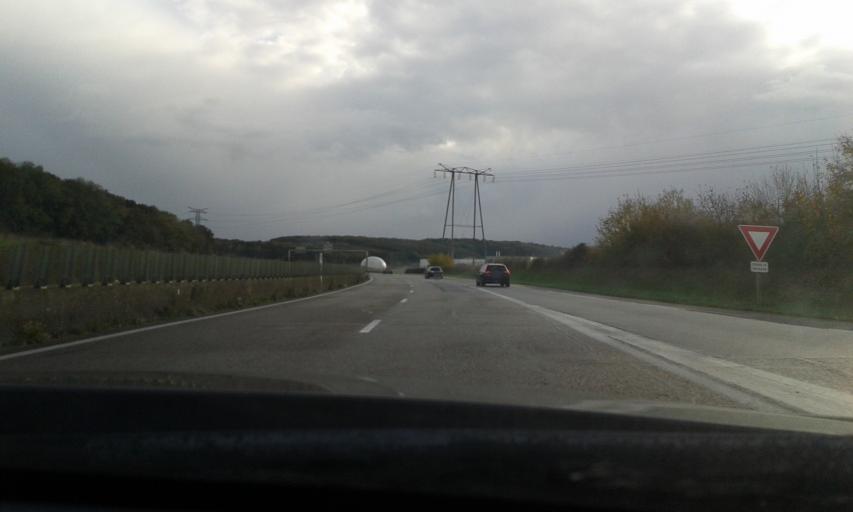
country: FR
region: Haute-Normandie
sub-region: Departement de l'Eure
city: Gravigny
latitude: 49.0589
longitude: 1.1744
